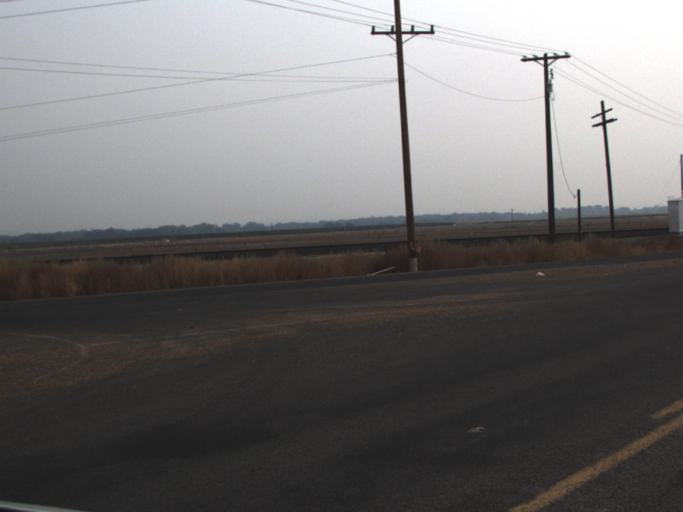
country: US
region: Washington
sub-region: Yakima County
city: Granger
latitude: 46.3277
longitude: -120.2367
